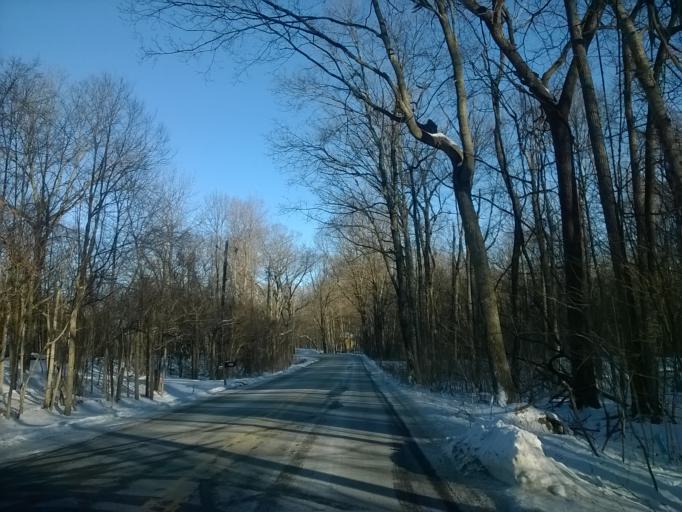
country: US
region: Indiana
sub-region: Boone County
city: Zionsville
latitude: 39.9245
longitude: -86.2848
